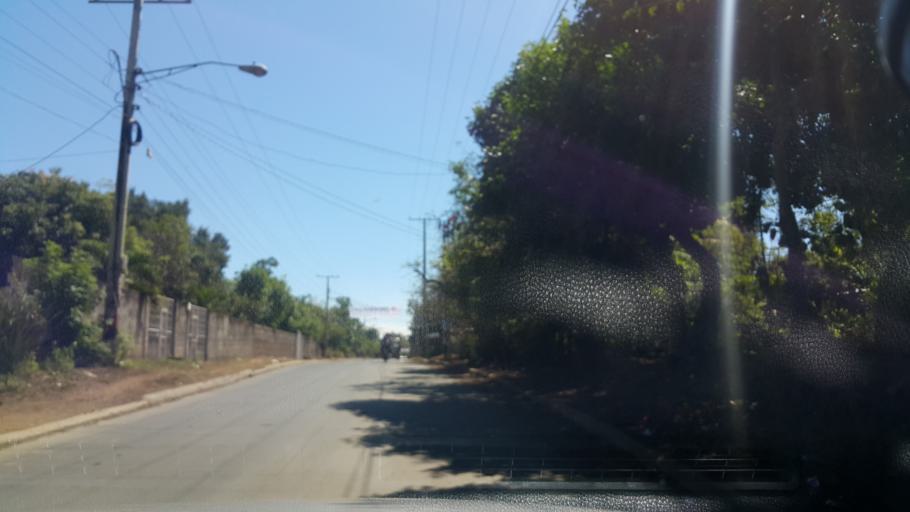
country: NI
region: Managua
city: Managua
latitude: 12.0931
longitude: -86.2021
